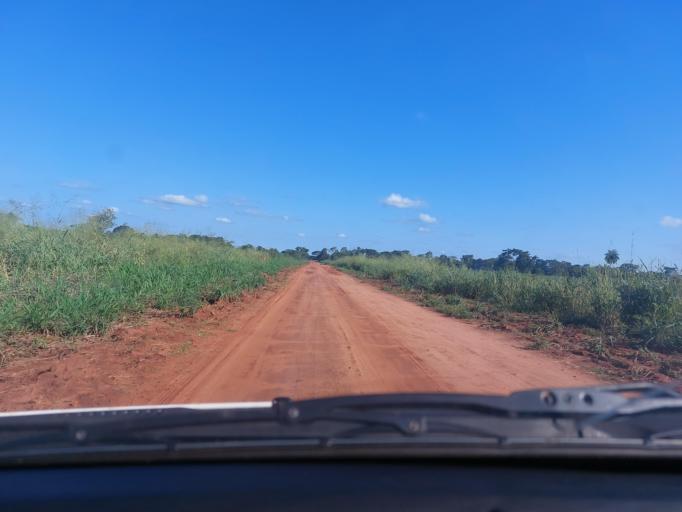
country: PY
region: San Pedro
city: Guayaybi
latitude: -24.5255
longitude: -56.5455
